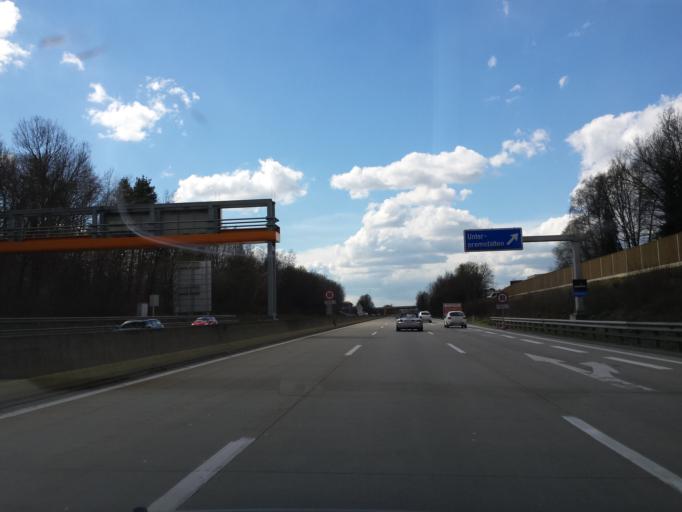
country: AT
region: Styria
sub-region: Politischer Bezirk Graz-Umgebung
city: Unterpremstatten
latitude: 46.9792
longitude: 15.3934
